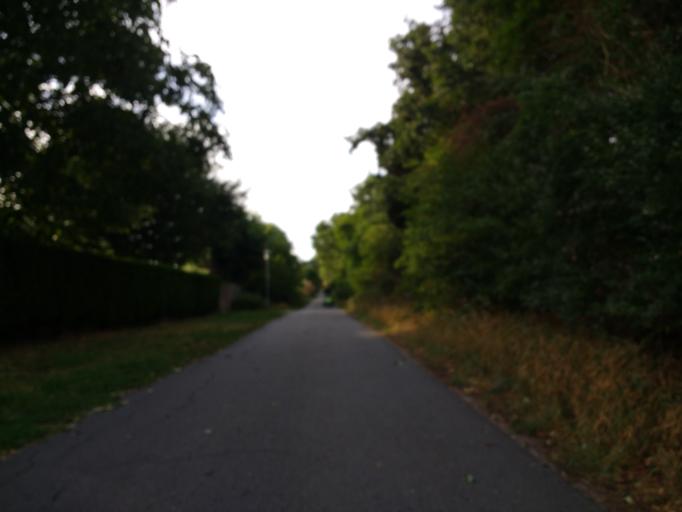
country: DE
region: Lower Saxony
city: Isenbuttel
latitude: 52.4439
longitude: 10.5630
